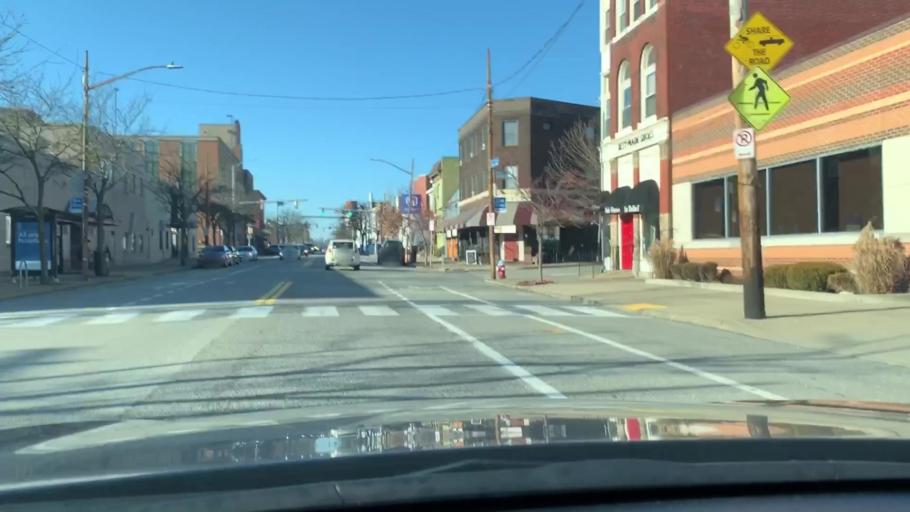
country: US
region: Pennsylvania
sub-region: Allegheny County
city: Bloomfield
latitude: 40.4578
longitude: -79.9419
